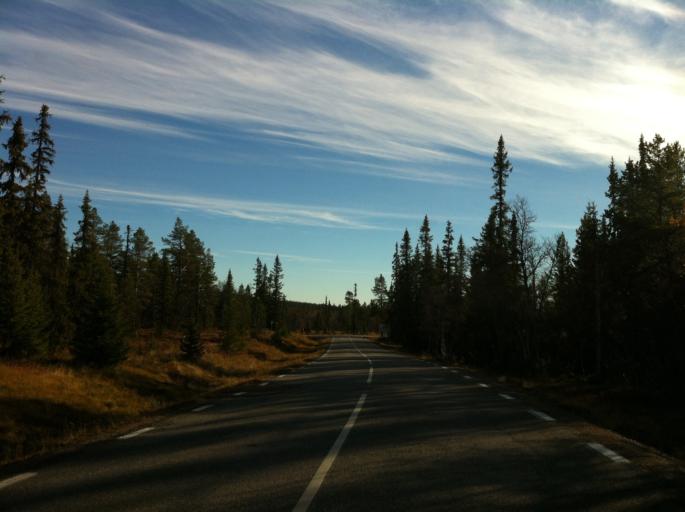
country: NO
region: Hedmark
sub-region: Engerdal
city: Engerdal
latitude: 62.0884
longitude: 12.3078
